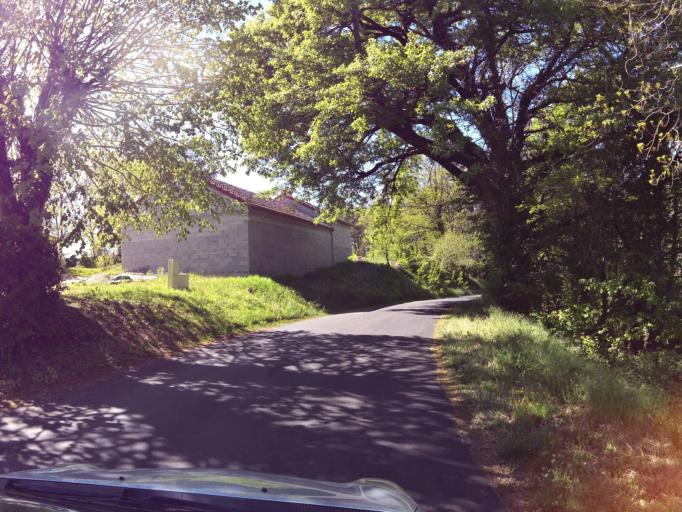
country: FR
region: Aquitaine
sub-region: Departement de la Dordogne
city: Sarlat-la-Caneda
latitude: 44.9574
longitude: 1.2315
